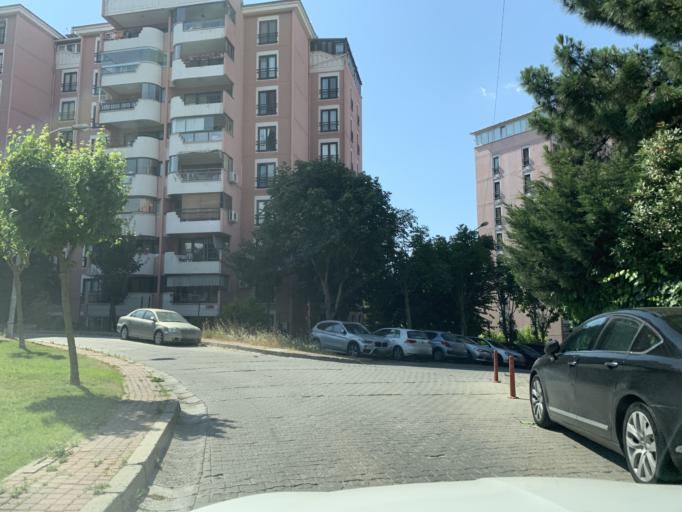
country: TR
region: Istanbul
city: Esenyurt
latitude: 41.0651
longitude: 28.6801
